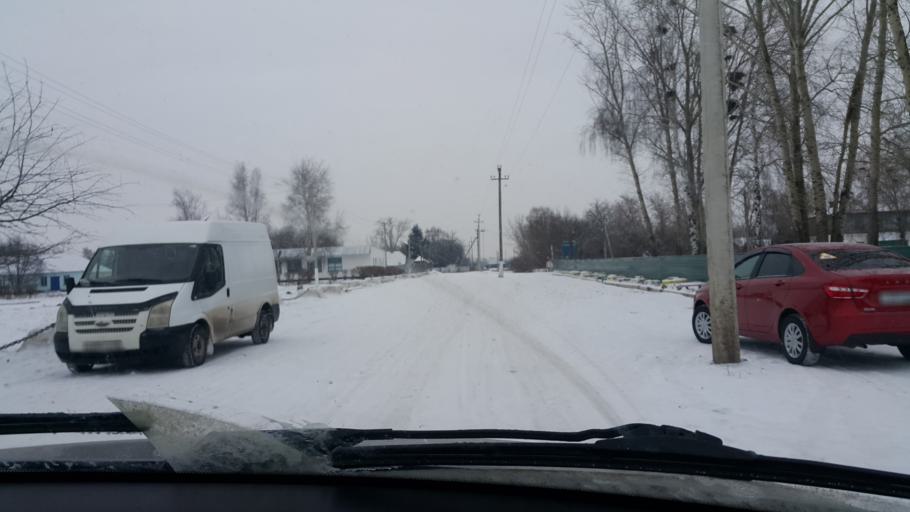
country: RU
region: Tambov
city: Inzhavino
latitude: 52.4687
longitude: 42.3822
